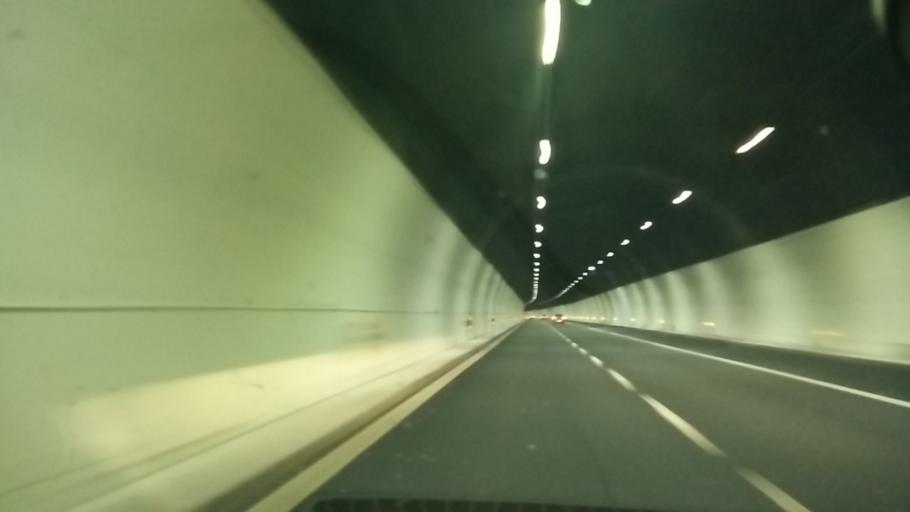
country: IT
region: Friuli Venezia Giulia
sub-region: Provincia di Udine
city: Bordano
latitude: 46.3375
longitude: 13.0711
